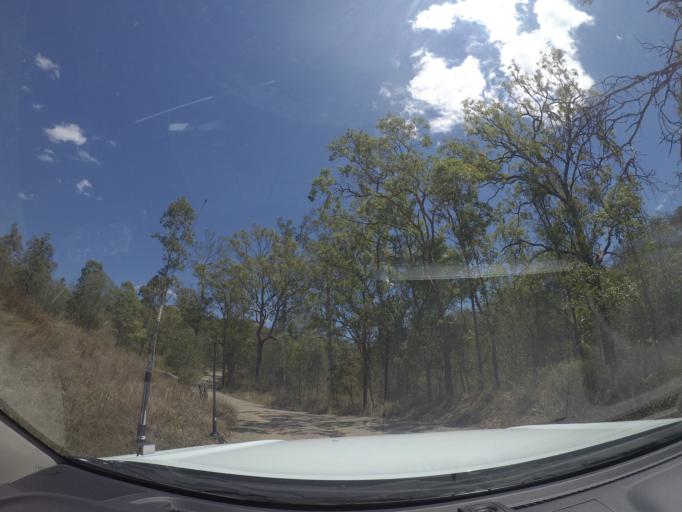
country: AU
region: Queensland
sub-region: Ipswich
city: Springfield Lakes
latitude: -27.8088
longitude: 152.8474
